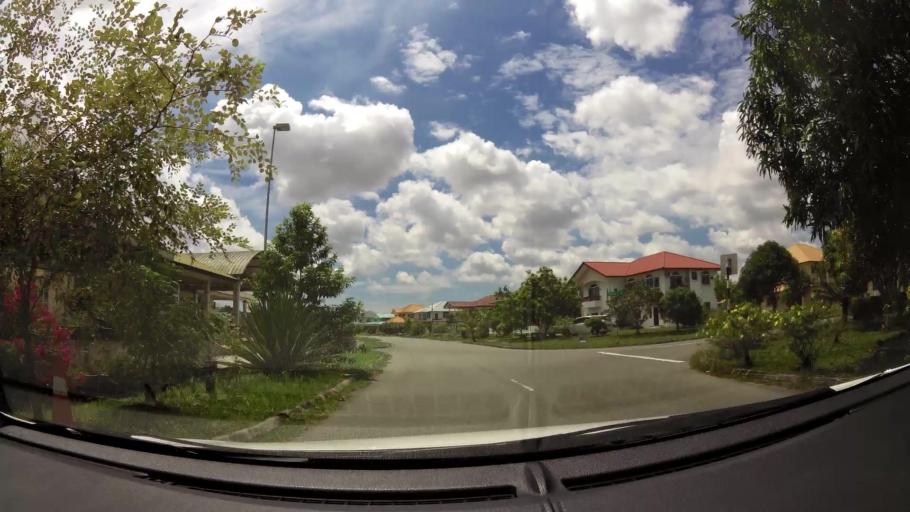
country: BN
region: Brunei and Muara
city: Bandar Seri Begawan
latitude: 4.9464
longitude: 114.9102
